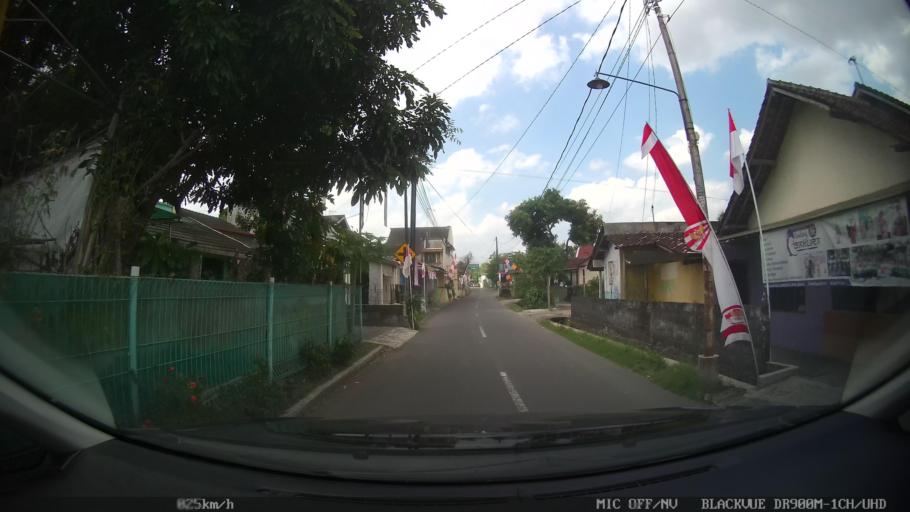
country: ID
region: Daerah Istimewa Yogyakarta
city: Yogyakarta
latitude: -7.7671
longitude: 110.3653
